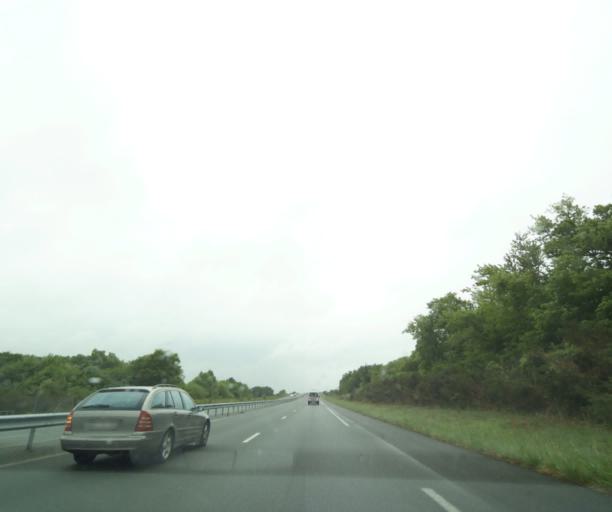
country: FR
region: Poitou-Charentes
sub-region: Departement de la Charente-Maritime
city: Nieul-les-Saintes
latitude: 45.7014
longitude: -0.7535
